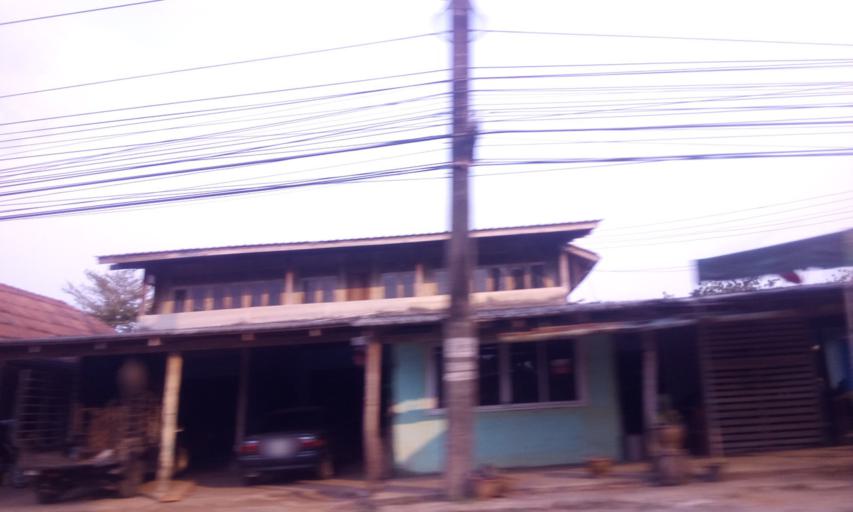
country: TH
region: Trat
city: Khao Saming
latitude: 12.2862
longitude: 102.3116
